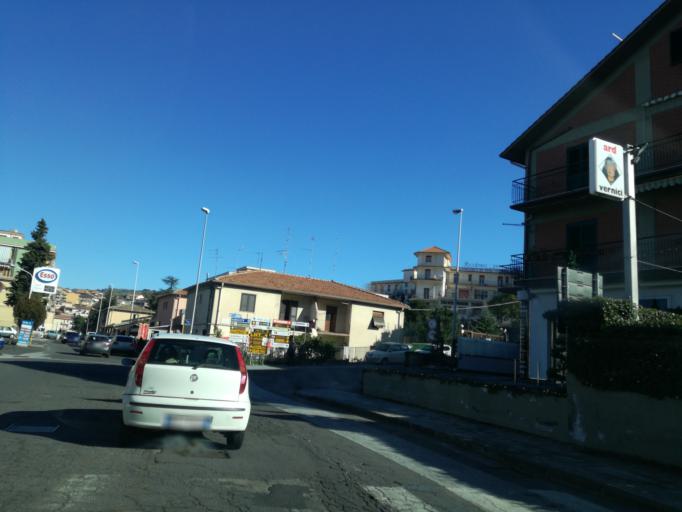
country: IT
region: Sicily
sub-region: Catania
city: Bronte
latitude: 37.7818
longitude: 14.8347
